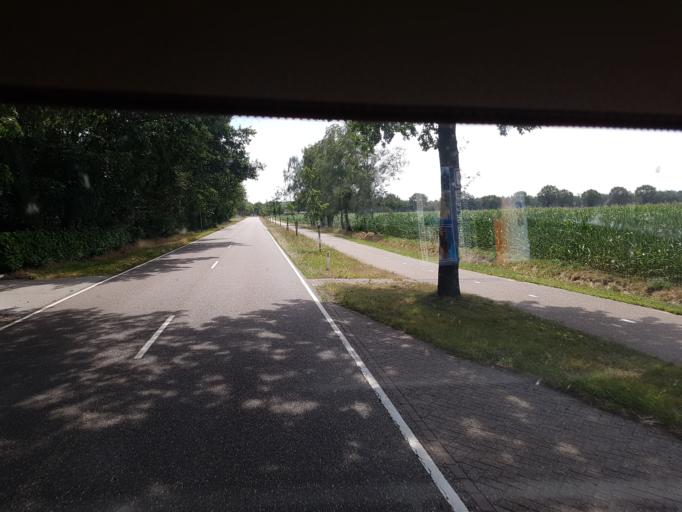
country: NL
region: Limburg
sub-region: Gemeente Nederweert
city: Nederweert
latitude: 51.2624
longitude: 5.7881
